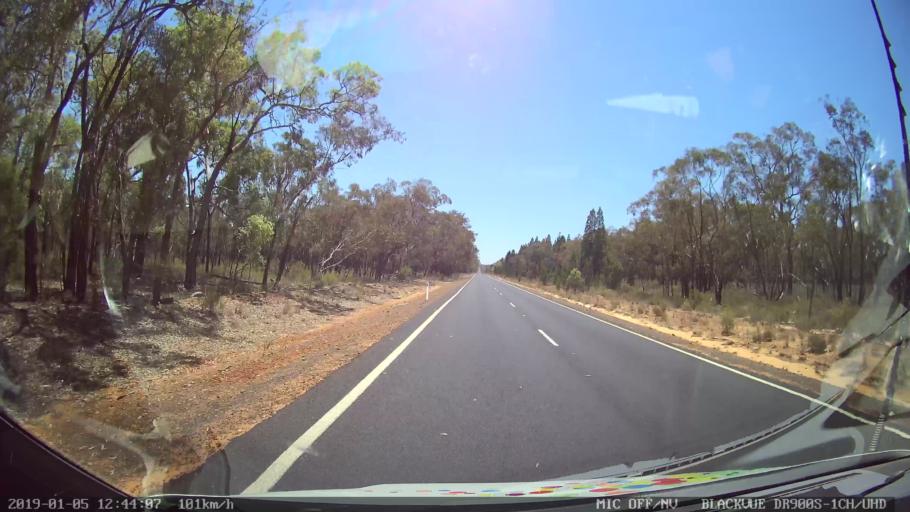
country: AU
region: New South Wales
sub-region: Warrumbungle Shire
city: Coonabarabran
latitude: -31.1409
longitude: 149.5332
